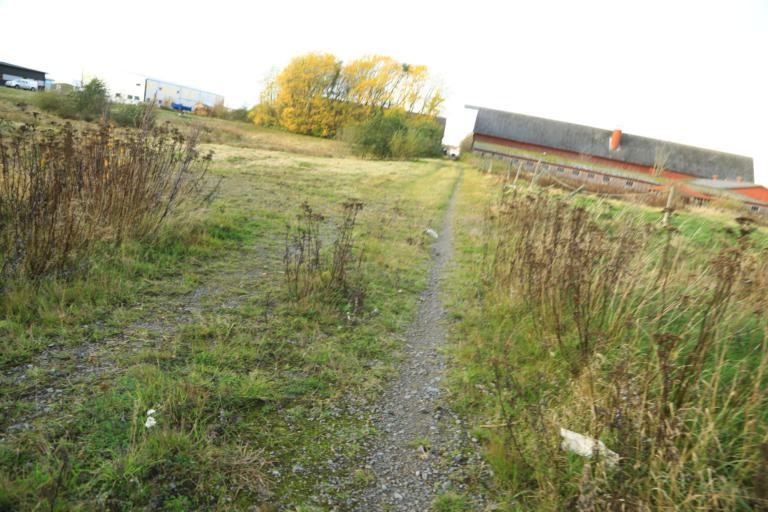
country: SE
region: Halland
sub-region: Varbergs Kommun
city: Varberg
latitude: 57.1222
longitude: 12.3038
